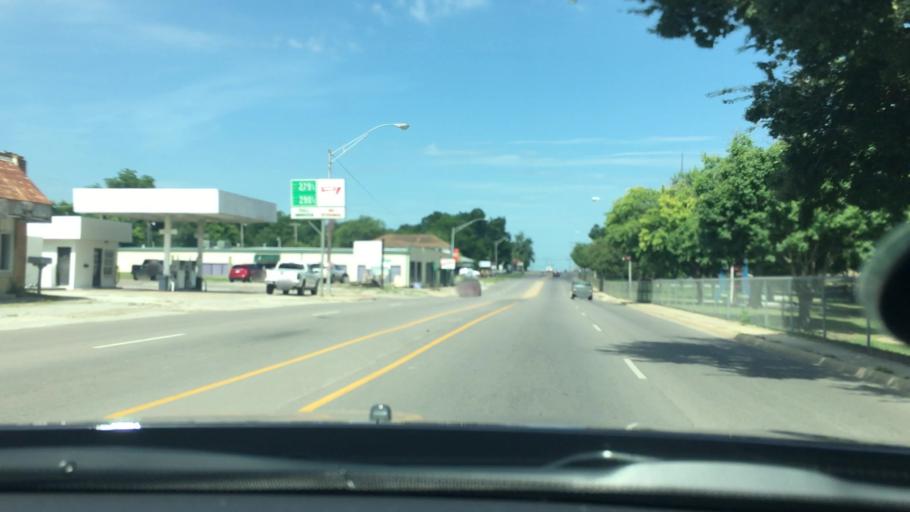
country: US
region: Oklahoma
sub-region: Pontotoc County
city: Ada
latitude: 34.7745
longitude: -96.6875
